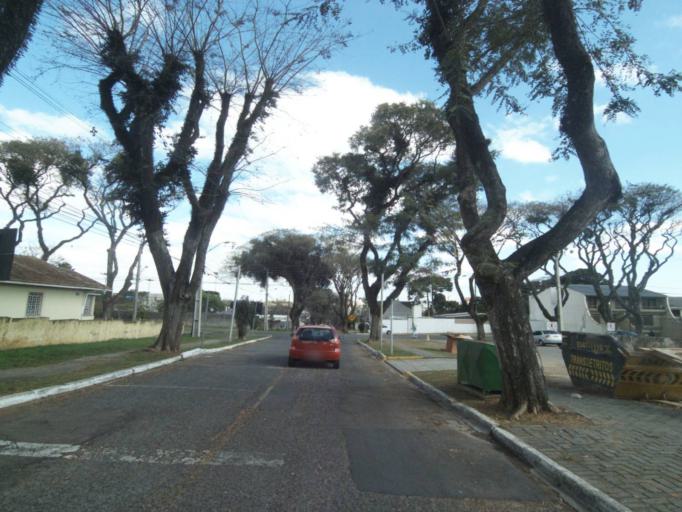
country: BR
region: Parana
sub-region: Curitiba
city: Curitiba
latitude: -25.4561
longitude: -49.2763
